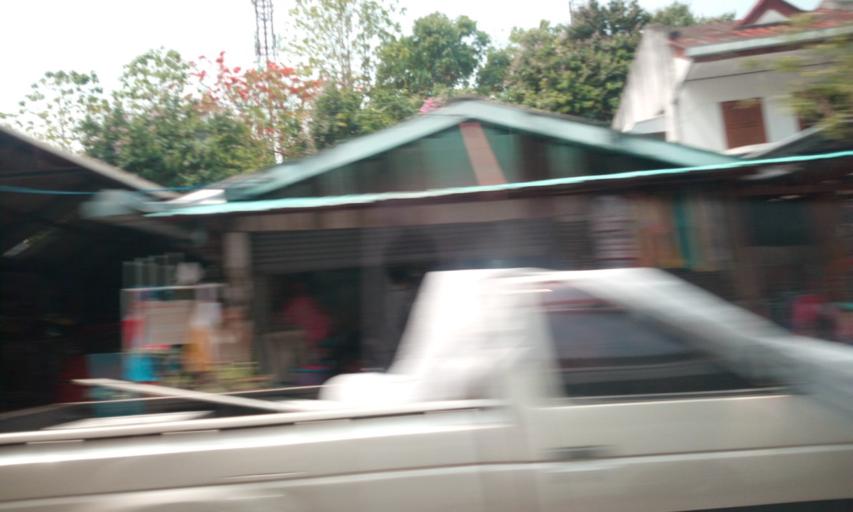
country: TH
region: Chiang Rai
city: Chiang Rai
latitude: 19.9112
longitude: 99.8258
